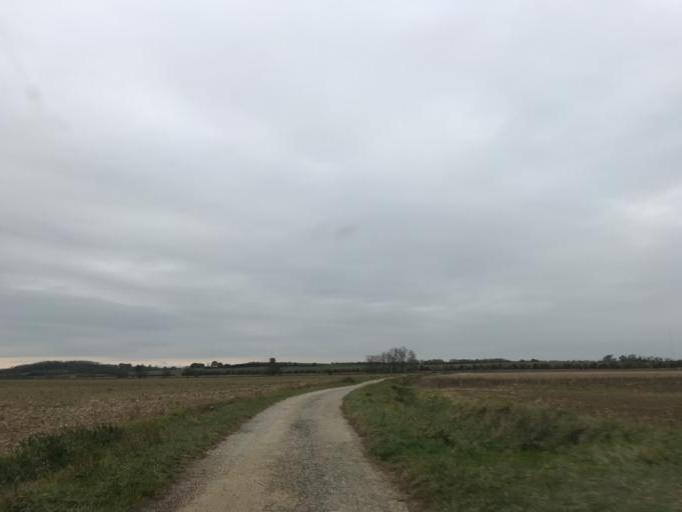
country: FR
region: Rhone-Alpes
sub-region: Departement de l'Ain
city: Miribel
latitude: 45.8405
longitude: 4.9578
